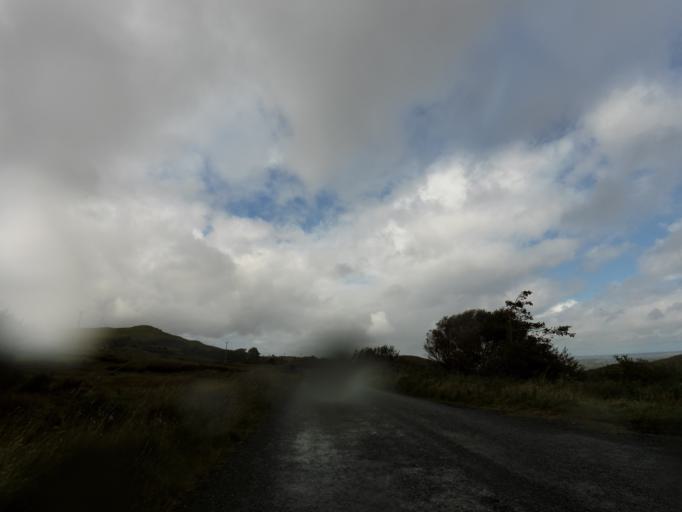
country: IE
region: Connaught
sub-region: County Galway
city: Oughterard
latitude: 53.4039
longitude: -9.3321
